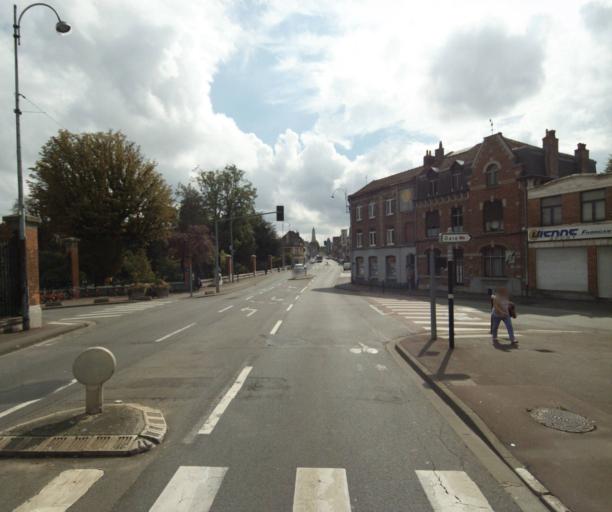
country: FR
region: Nord-Pas-de-Calais
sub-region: Departement du Nord
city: Marcq-en-Baroeul
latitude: 50.6597
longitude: 3.0738
